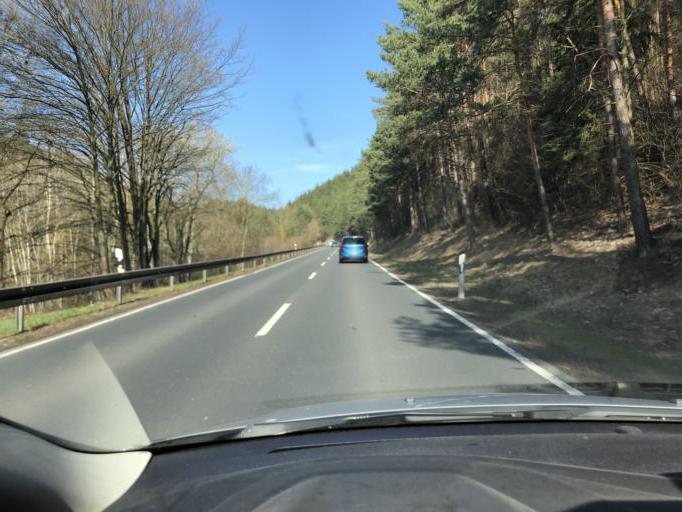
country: DE
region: Thuringia
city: Schwarza
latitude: 50.7957
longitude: 11.3119
